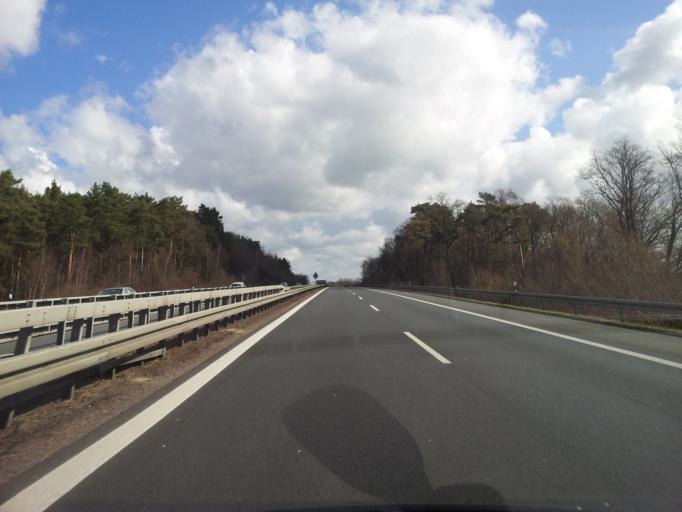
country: DE
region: Saxony
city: Albertstadt
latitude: 51.1454
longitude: 13.7661
